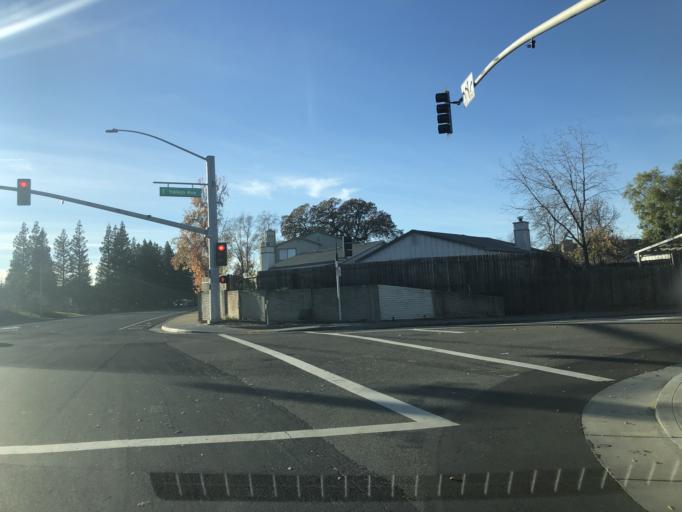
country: US
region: California
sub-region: Placer County
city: Roseville
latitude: 38.7594
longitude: -121.2980
